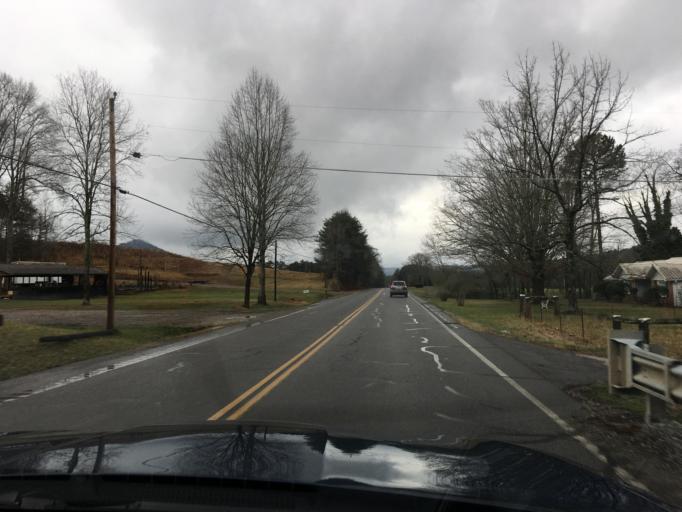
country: US
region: Tennessee
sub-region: Polk County
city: Benton
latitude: 35.1203
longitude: -84.6508
